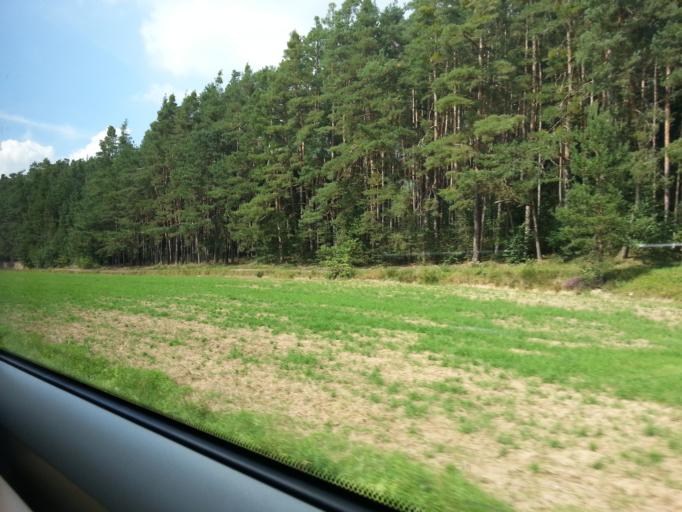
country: DE
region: Bavaria
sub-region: Regierungsbezirk Mittelfranken
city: Absberg
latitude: 49.1174
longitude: 10.8908
